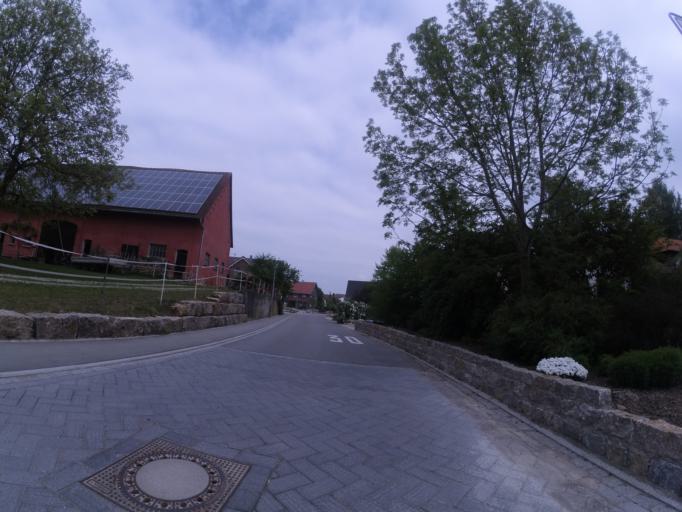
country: DE
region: Baden-Wuerttemberg
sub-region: Tuebingen Region
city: Staig
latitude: 48.3006
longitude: 10.0018
